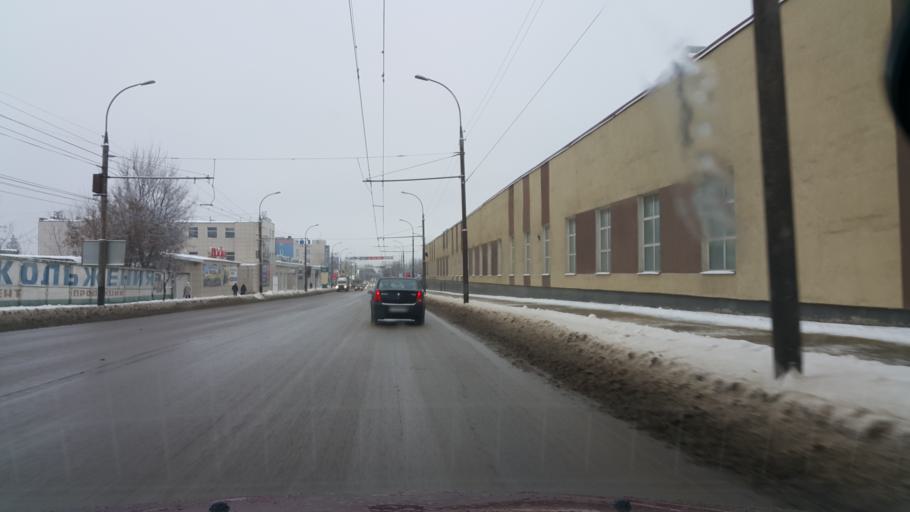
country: RU
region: Tambov
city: Tambov
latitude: 52.7238
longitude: 41.4310
